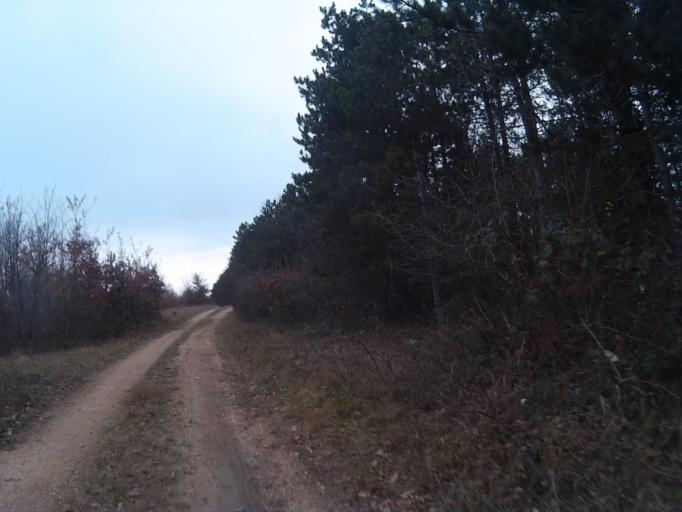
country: HU
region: Veszprem
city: Tapolca
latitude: 46.9763
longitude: 17.4902
